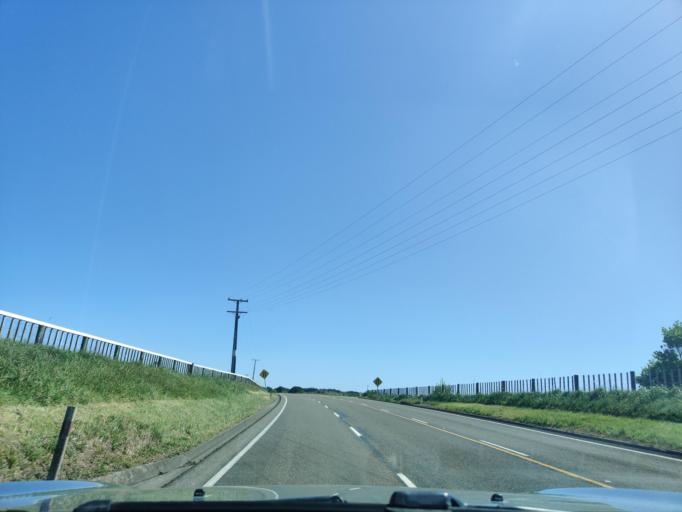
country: NZ
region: Manawatu-Wanganui
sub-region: Wanganui District
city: Wanganui
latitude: -39.8191
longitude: 174.8346
